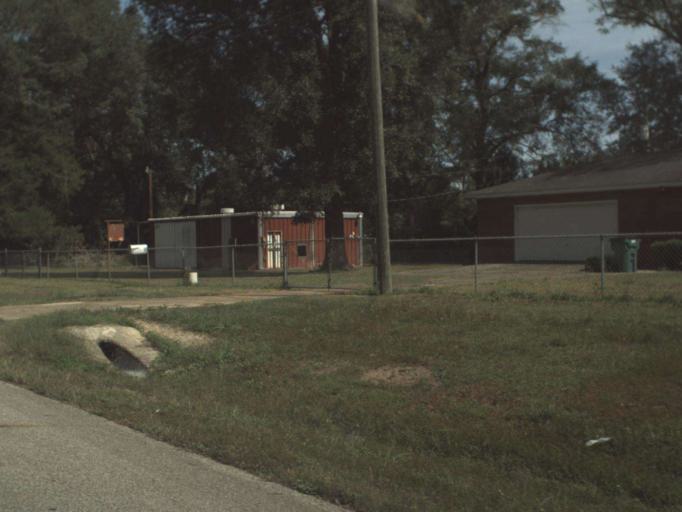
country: US
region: Florida
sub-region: Jackson County
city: Graceville
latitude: 30.9303
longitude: -85.5191
